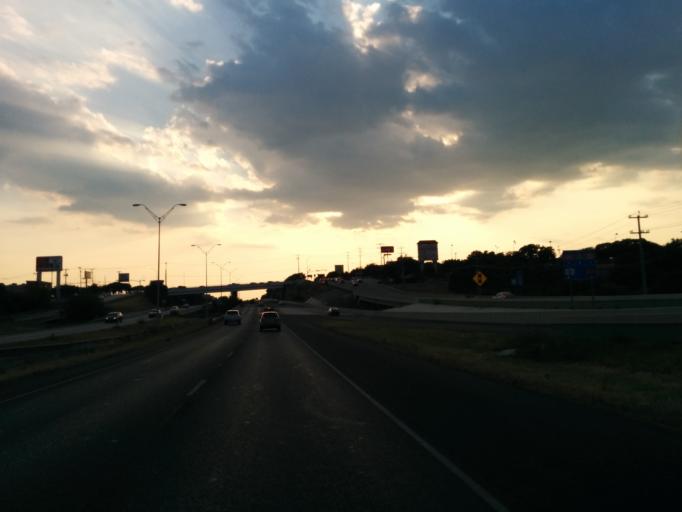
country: US
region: Texas
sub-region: Bexar County
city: Hollywood Park
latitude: 29.6087
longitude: -98.5050
